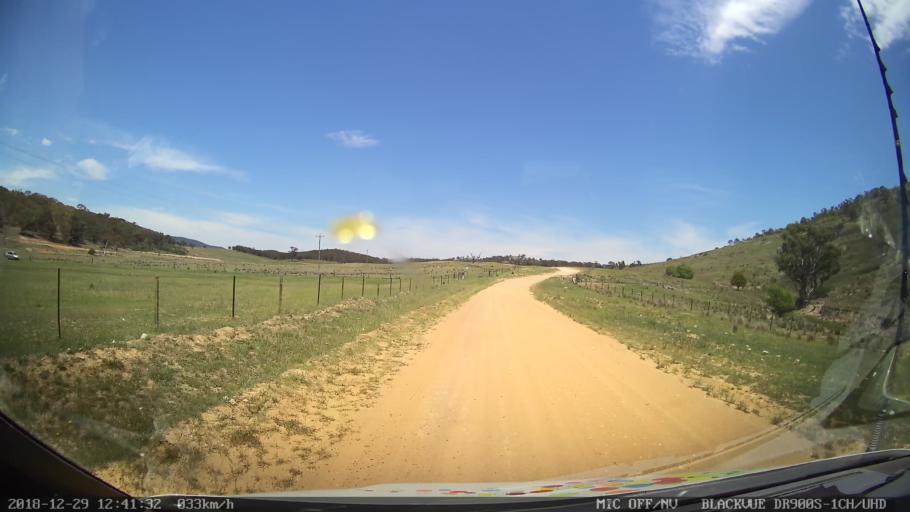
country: AU
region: Australian Capital Territory
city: Macarthur
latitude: -35.6083
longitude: 149.2222
